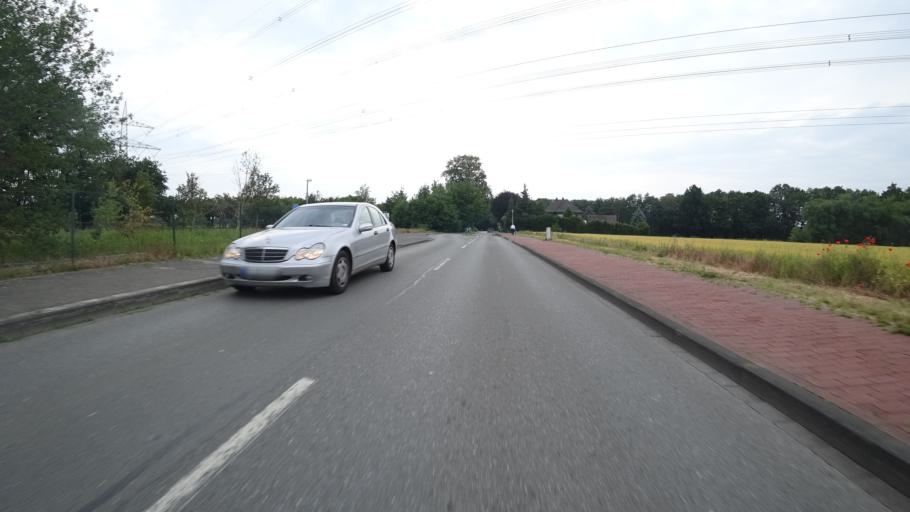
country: DE
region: North Rhine-Westphalia
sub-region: Regierungsbezirk Detmold
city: Guetersloh
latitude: 51.9318
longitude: 8.3834
